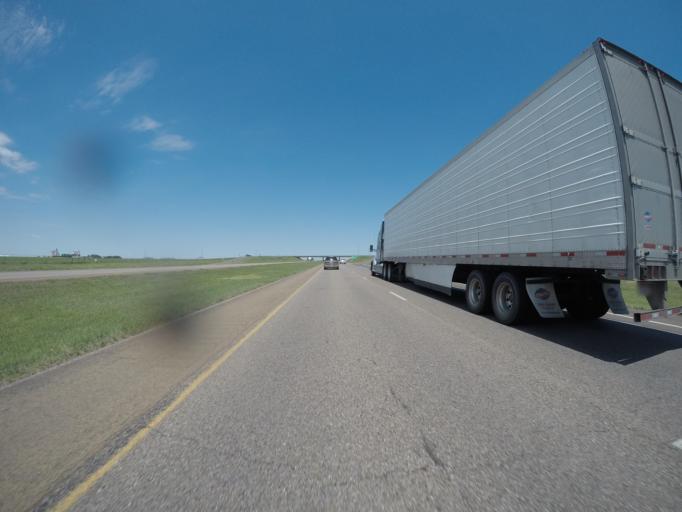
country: US
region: Kansas
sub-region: Logan County
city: Oakley
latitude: 39.2753
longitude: -100.9394
